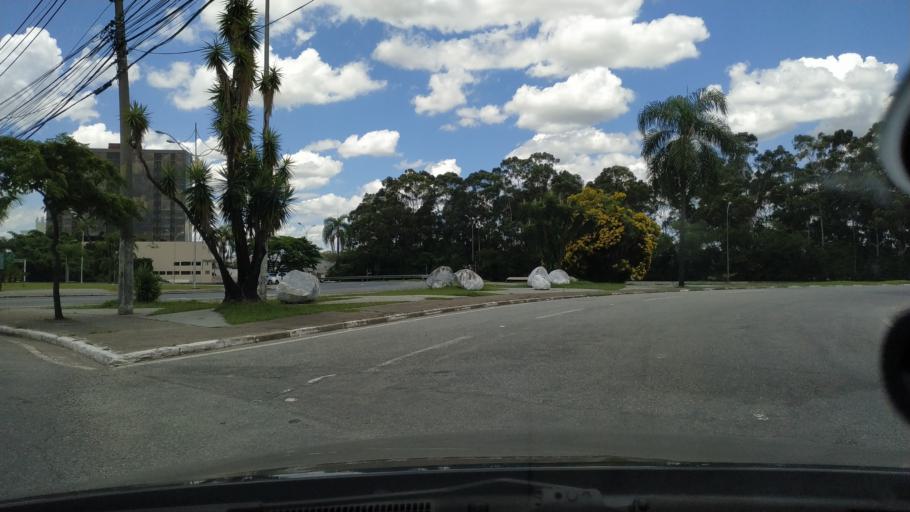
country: BR
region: Sao Paulo
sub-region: Barueri
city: Barueri
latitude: -23.5041
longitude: -46.8791
